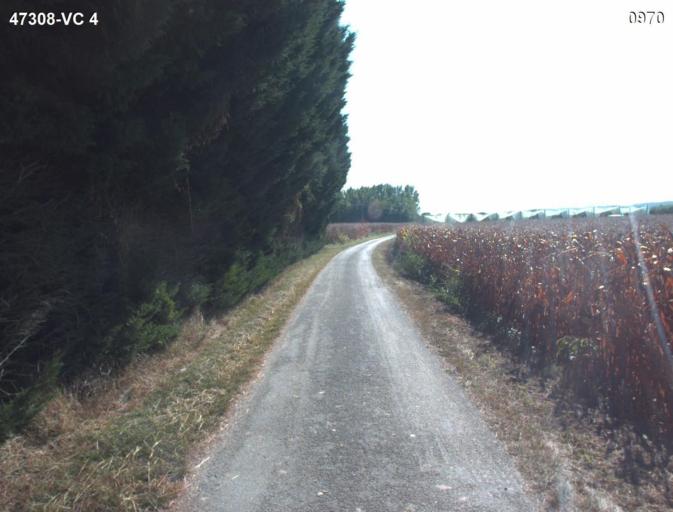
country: FR
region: Aquitaine
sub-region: Departement du Lot-et-Garonne
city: Buzet-sur-Baise
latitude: 44.2632
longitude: 0.3322
